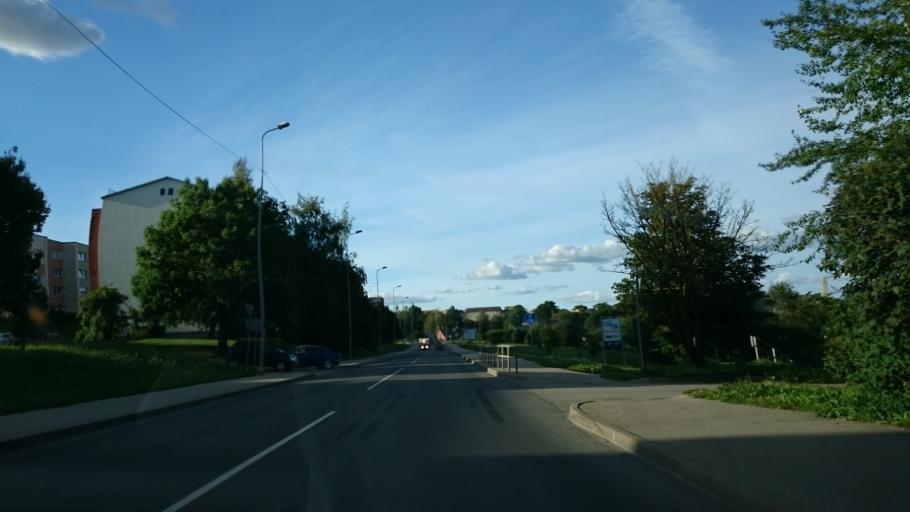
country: LV
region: Saldus Rajons
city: Saldus
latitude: 56.6609
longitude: 22.4760
